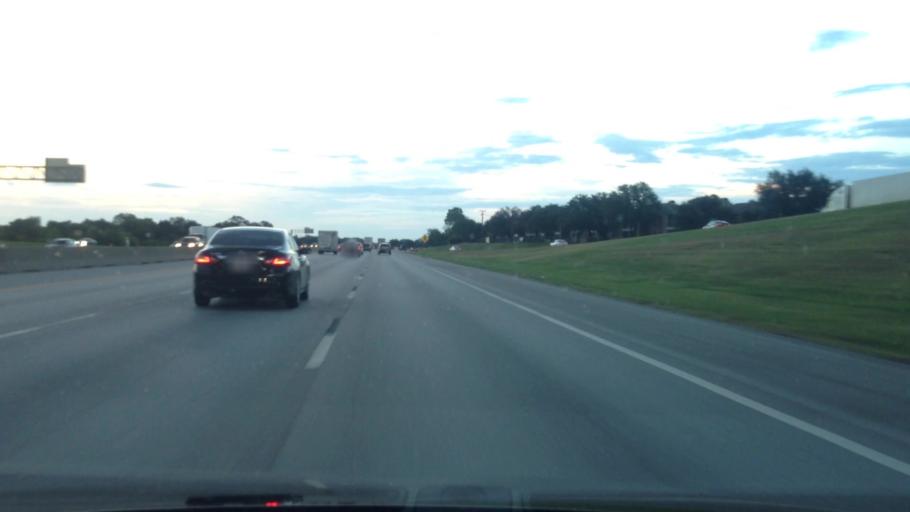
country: US
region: Texas
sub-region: Tarrant County
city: Pantego
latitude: 32.7600
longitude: -97.1669
